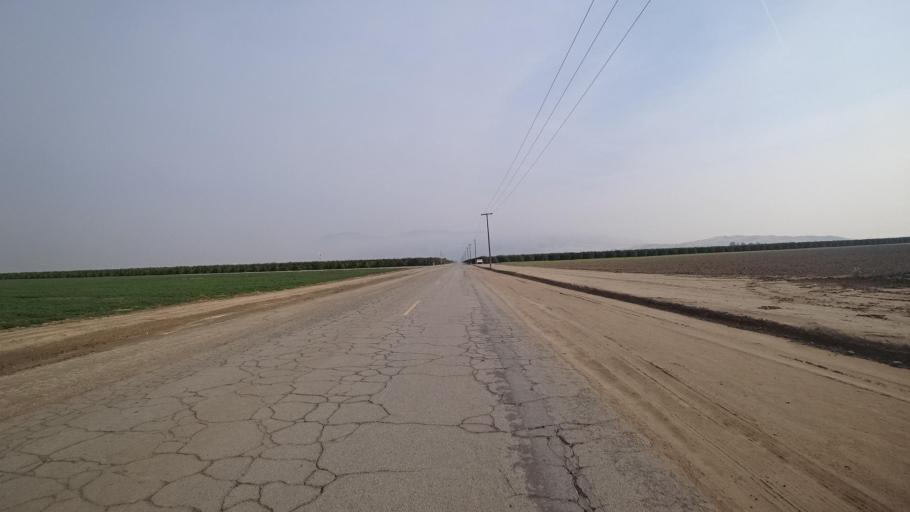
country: US
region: California
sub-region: Kern County
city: Arvin
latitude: 35.1509
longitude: -118.8616
